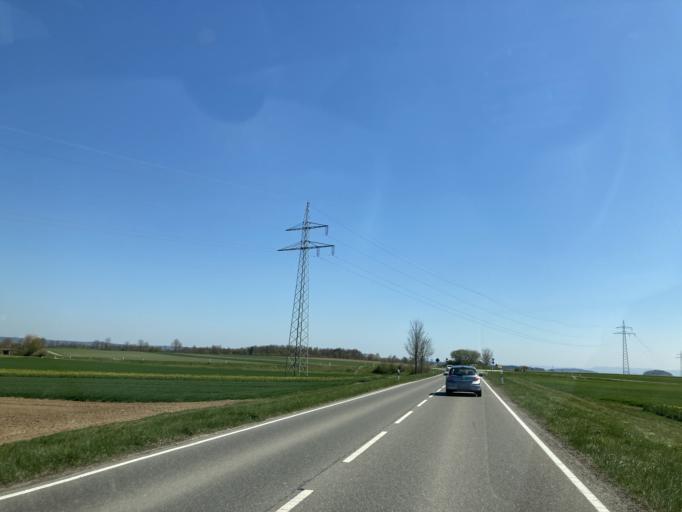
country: DE
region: Baden-Wuerttemberg
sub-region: Regierungsbezirk Stuttgart
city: Bondorf
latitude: 48.4980
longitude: 8.8423
